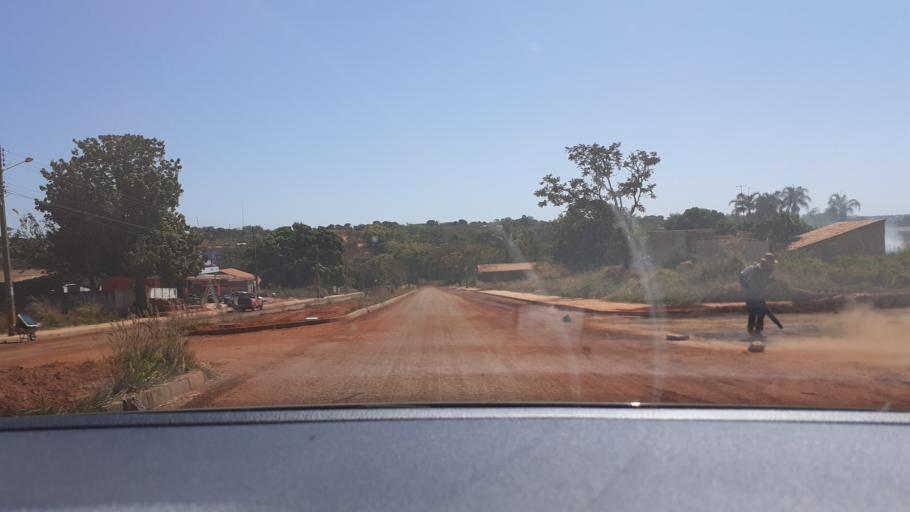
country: BR
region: Goias
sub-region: Aparecida De Goiania
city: Aparecida de Goiania
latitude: -16.8759
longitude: -49.2563
